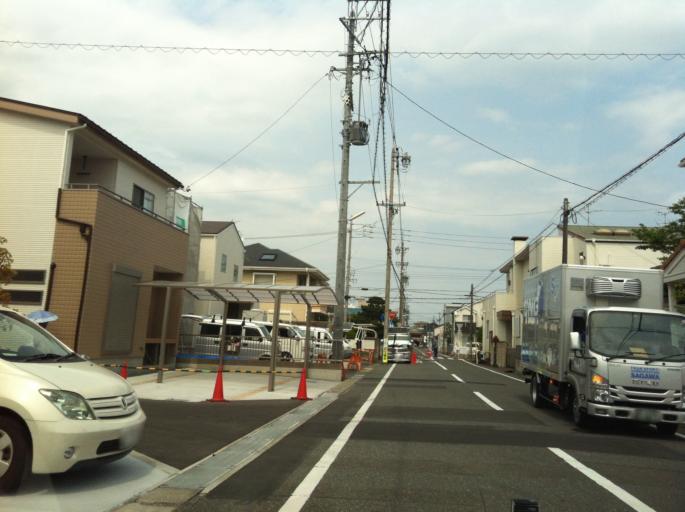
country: JP
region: Shizuoka
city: Shizuoka-shi
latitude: 35.0167
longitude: 138.4720
